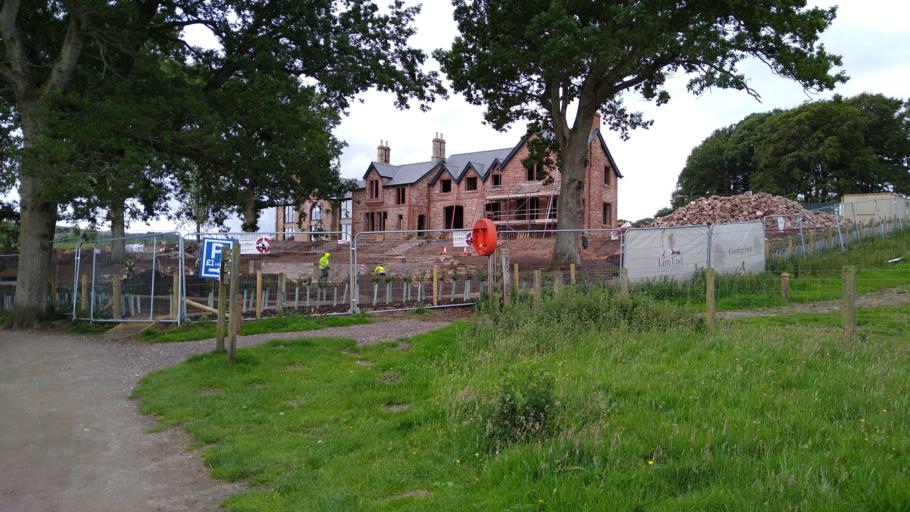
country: GB
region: England
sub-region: Cumbria
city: Brampton
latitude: 54.9184
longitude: -2.7136
